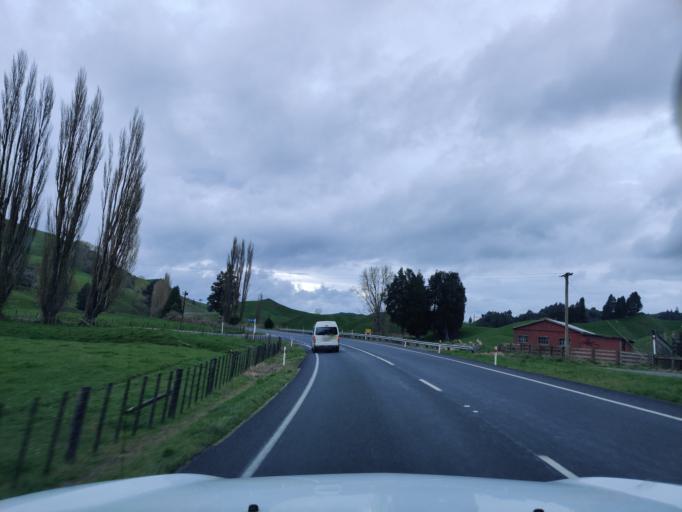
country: NZ
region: Waikato
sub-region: Otorohanga District
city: Otorohanga
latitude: -38.4737
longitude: 175.1740
